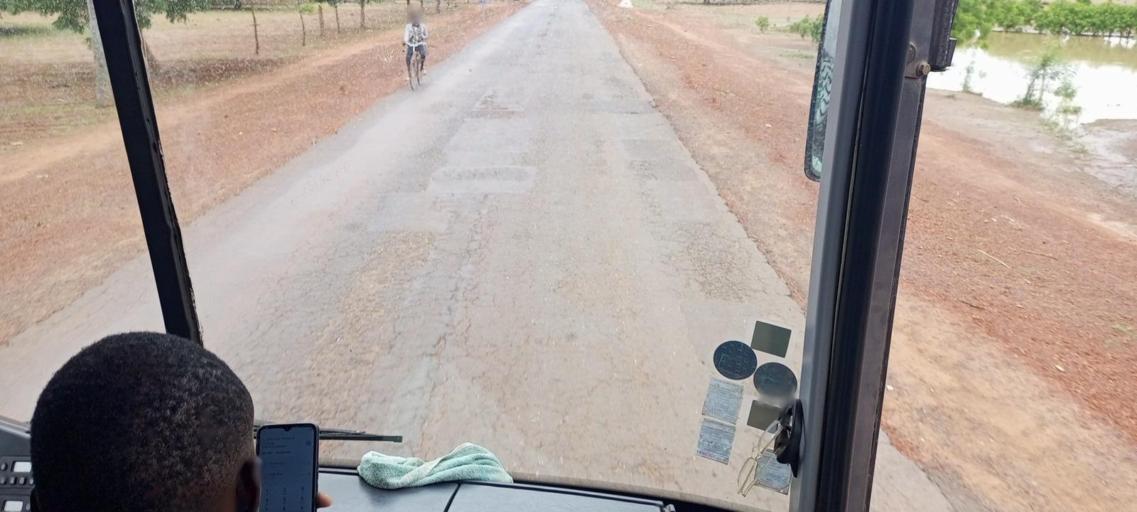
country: ML
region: Sikasso
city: Koutiala
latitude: 12.5799
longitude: -5.6100
